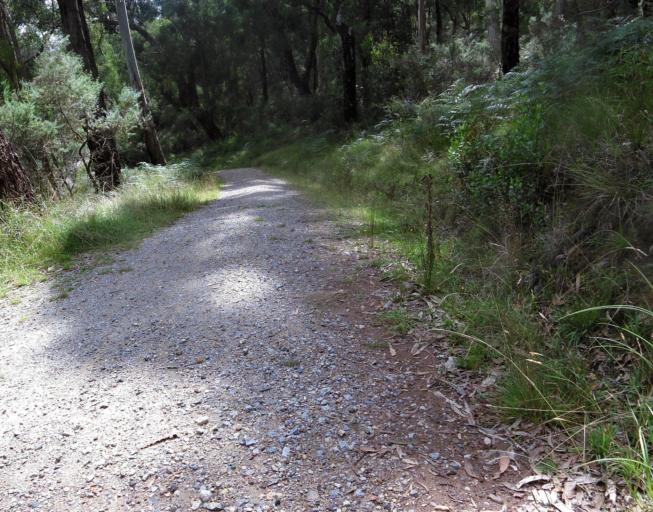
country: AU
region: Victoria
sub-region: Yarra Ranges
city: Montrose
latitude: -37.8299
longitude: 145.3442
